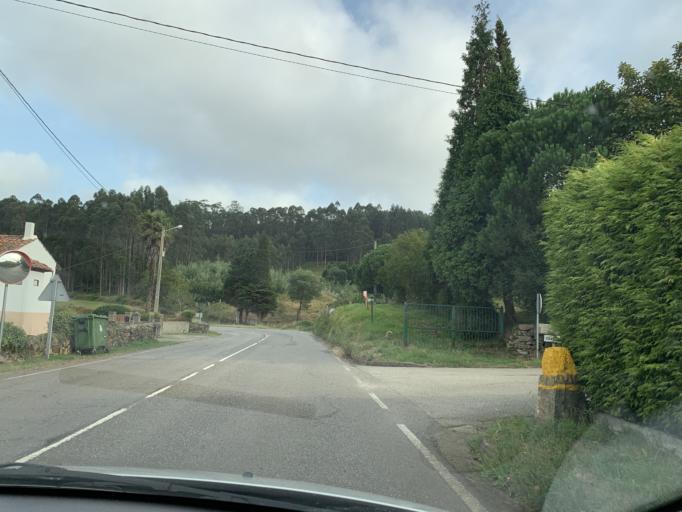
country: ES
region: Asturias
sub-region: Province of Asturias
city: Villaviciosa
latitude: 43.5189
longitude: -5.4387
